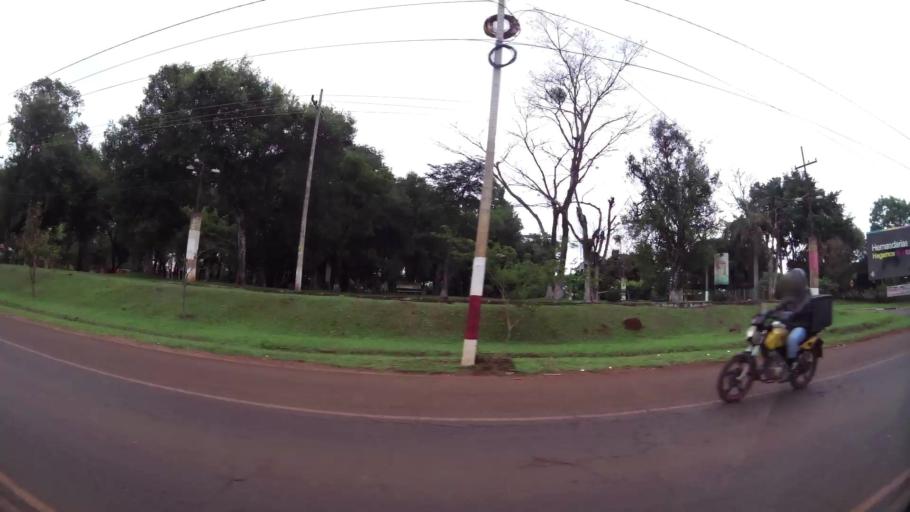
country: PY
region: Alto Parana
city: Ciudad del Este
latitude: -25.4112
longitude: -54.6340
